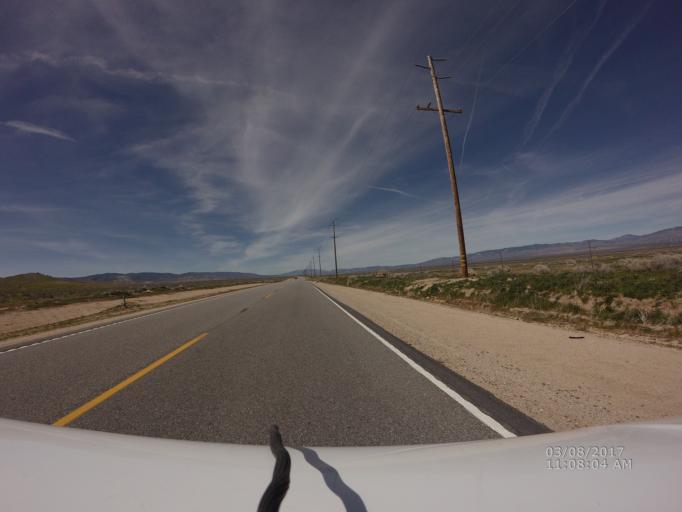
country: US
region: California
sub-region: Los Angeles County
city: Green Valley
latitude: 34.7755
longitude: -118.3835
